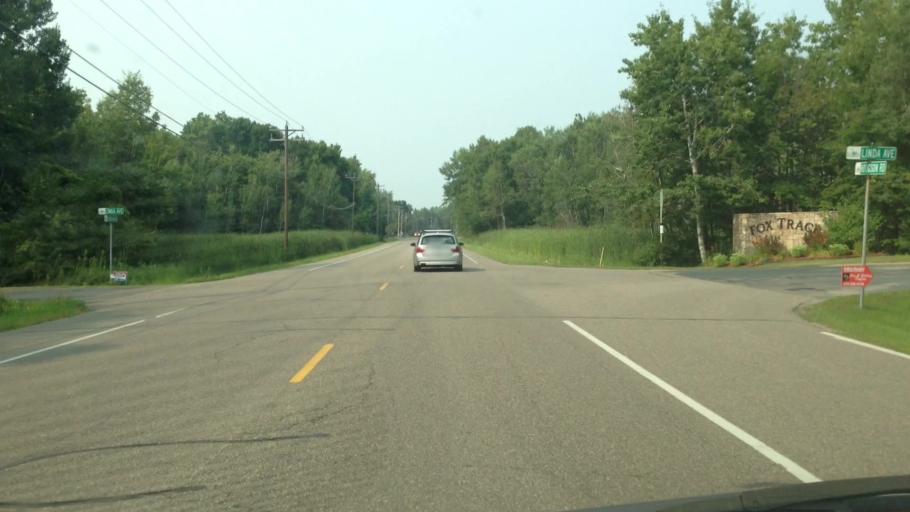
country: US
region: Minnesota
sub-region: Anoka County
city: Circle Pines
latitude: 45.1319
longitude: -93.1273
